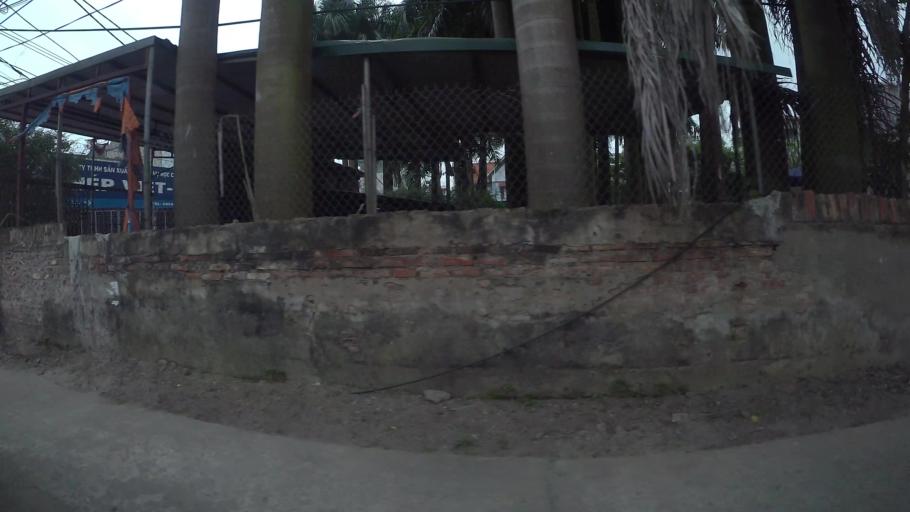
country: VN
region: Ha Noi
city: Trau Quy
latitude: 21.0510
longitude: 105.9247
